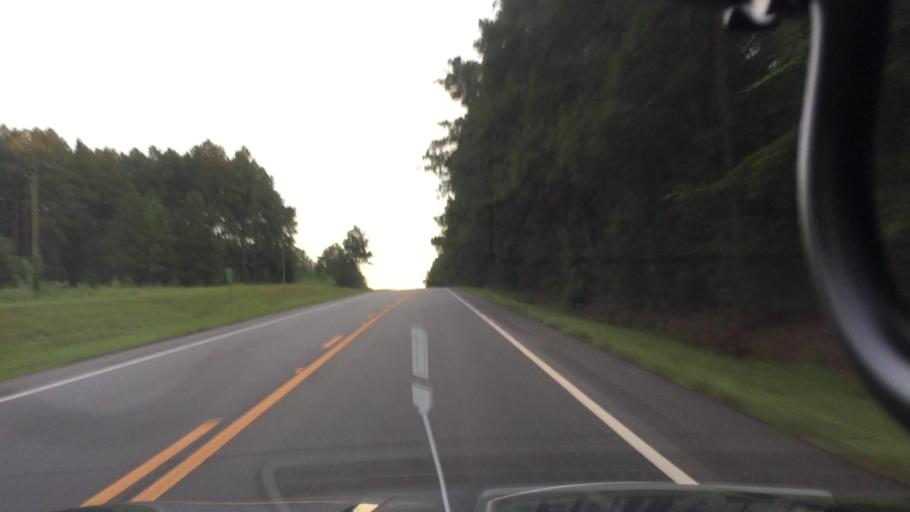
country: US
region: Alabama
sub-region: Coffee County
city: New Brockton
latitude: 31.5189
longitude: -85.9172
